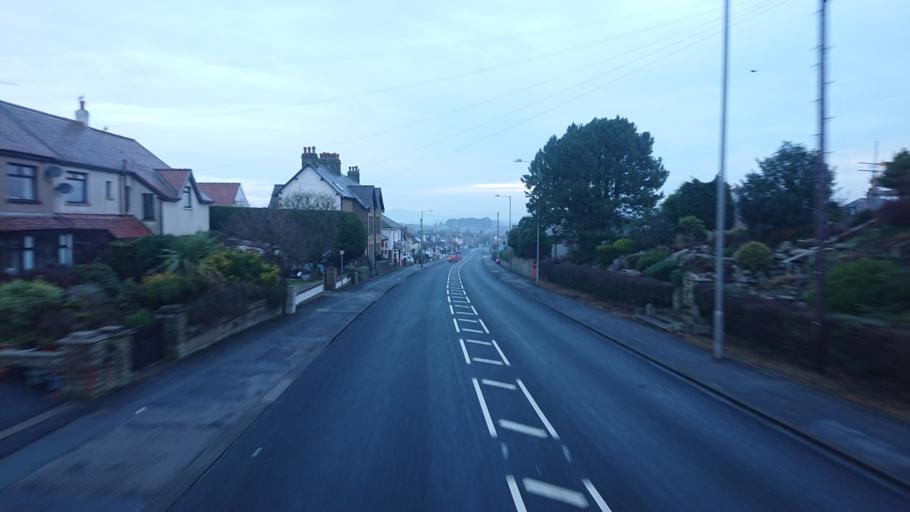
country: GB
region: England
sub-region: Lancashire
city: Bolton le Sands
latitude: 54.0889
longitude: -2.8164
